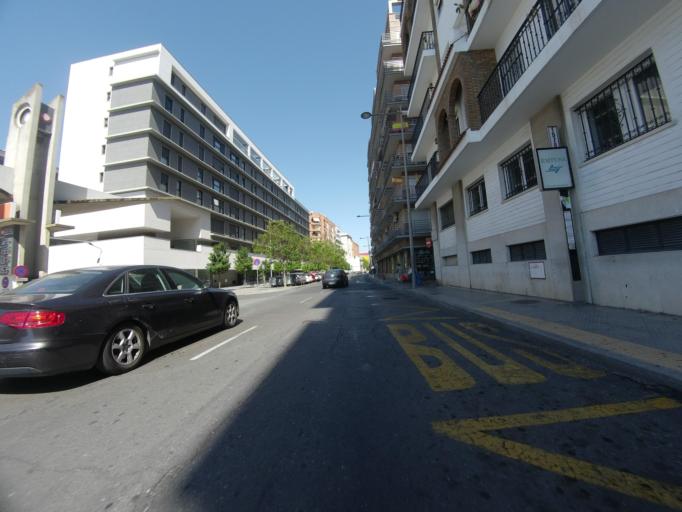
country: ES
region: Andalusia
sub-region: Provincia de Huelva
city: Huelva
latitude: 37.2538
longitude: -6.9518
